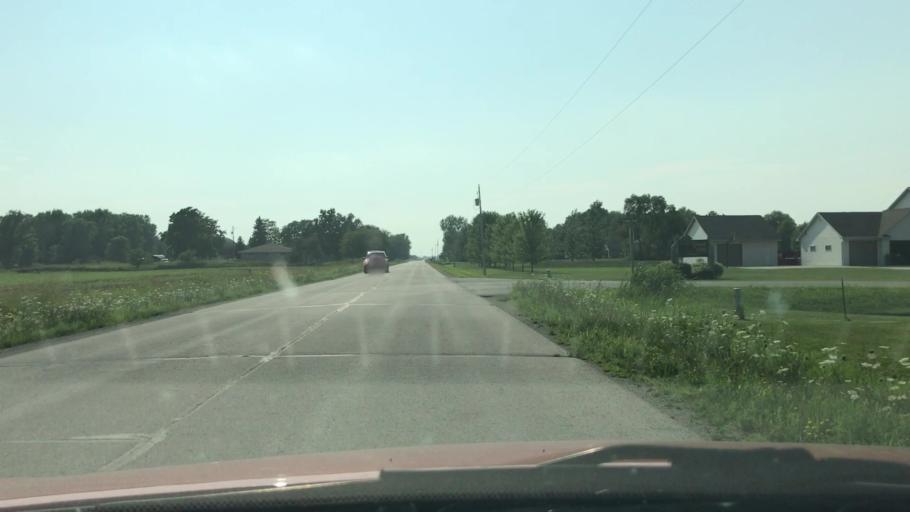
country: US
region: Wisconsin
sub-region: Brown County
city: Oneida
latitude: 44.4298
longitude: -88.1619
